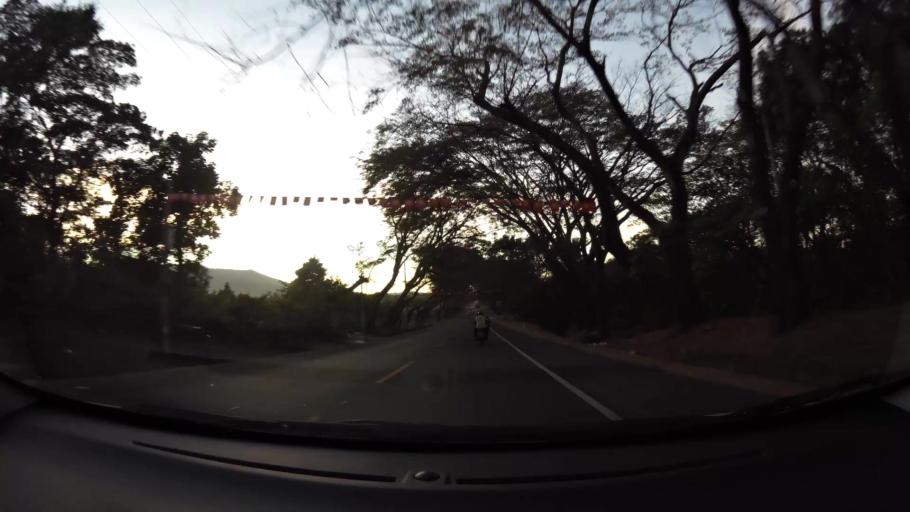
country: SV
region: San Miguel
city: Moncagua
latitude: 13.5035
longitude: -88.2237
